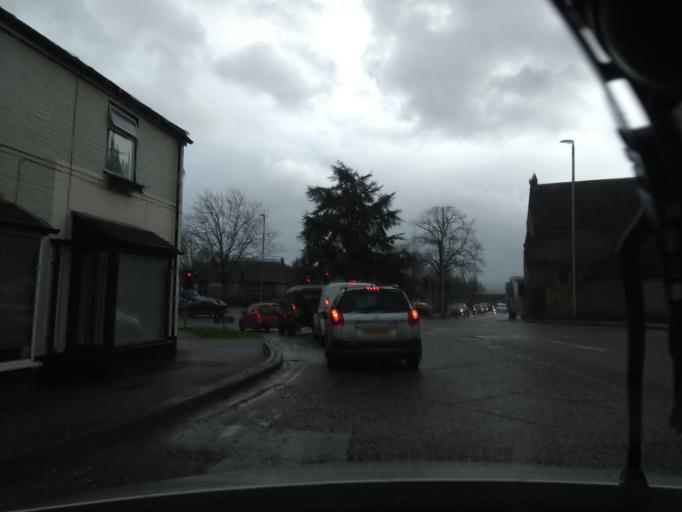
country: GB
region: England
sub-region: Somerset
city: Taunton
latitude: 51.0259
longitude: -3.1044
